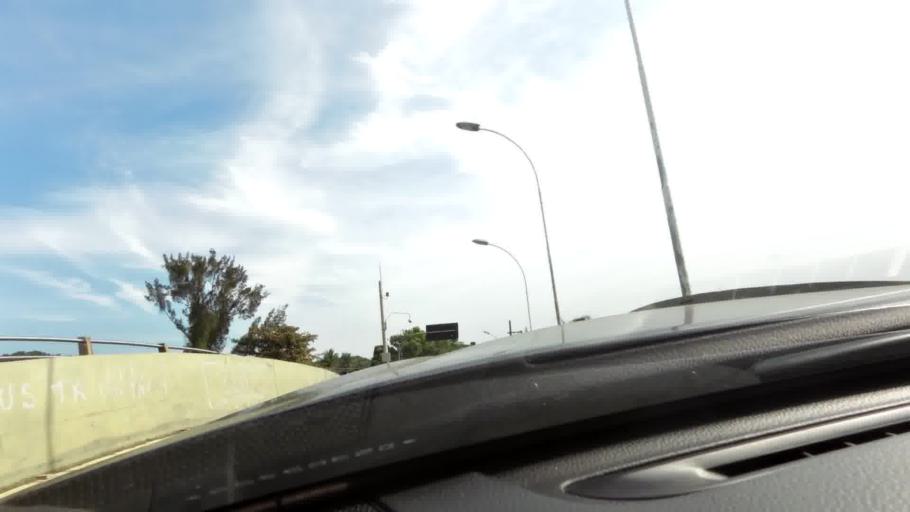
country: BR
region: Espirito Santo
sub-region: Guarapari
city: Guarapari
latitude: -20.6260
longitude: -40.4689
